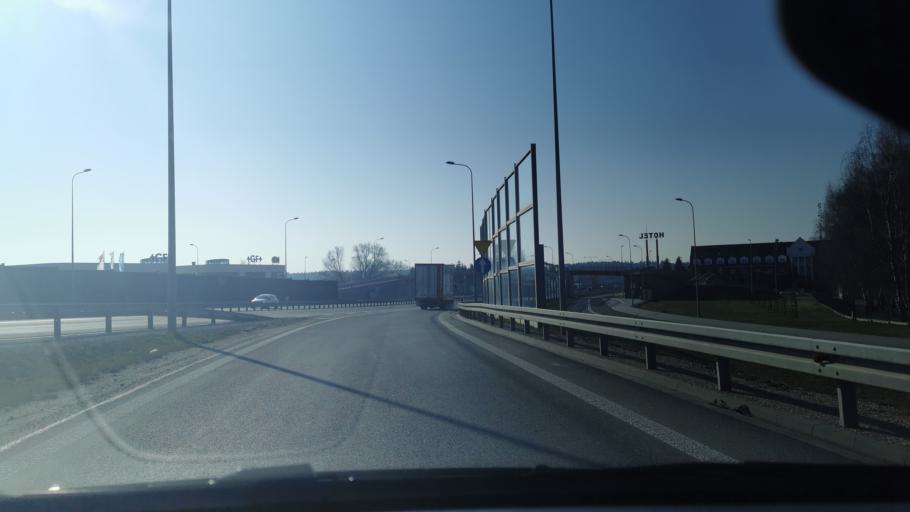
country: PL
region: Masovian Voivodeship
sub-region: Powiat piaseczynski
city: Lesznowola
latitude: 52.1126
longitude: 20.8892
